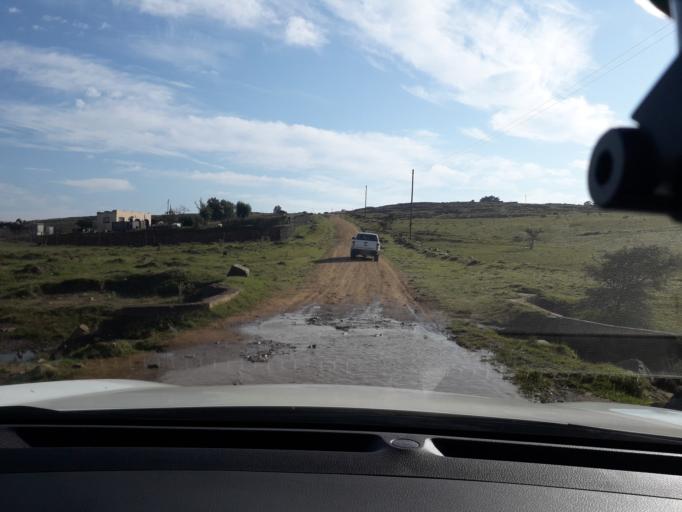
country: ZA
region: Eastern Cape
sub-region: Buffalo City Metropolitan Municipality
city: Bhisho
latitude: -32.9444
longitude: 27.2895
